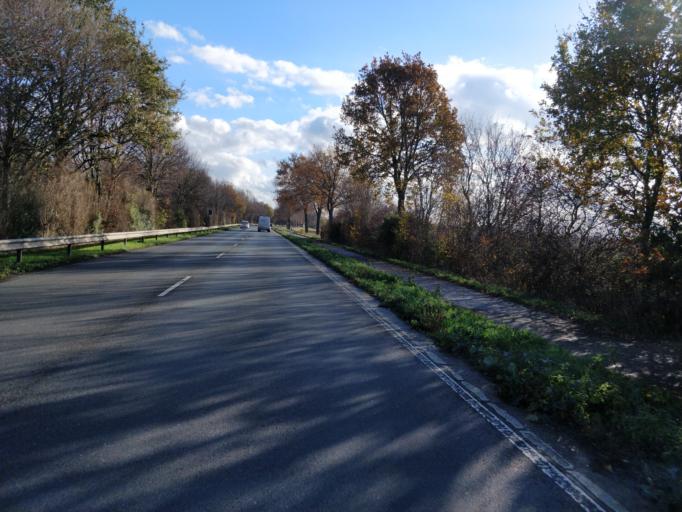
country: DE
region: North Rhine-Westphalia
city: Rees
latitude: 51.7836
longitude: 6.3751
